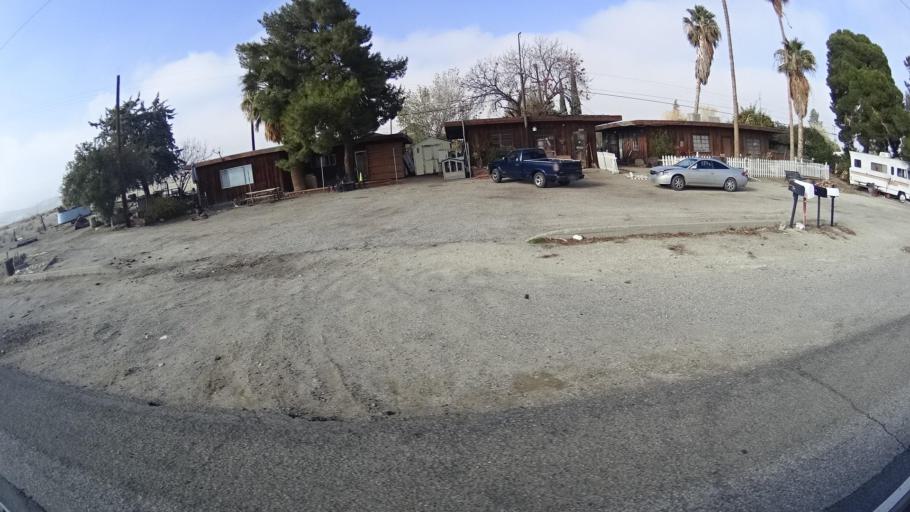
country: US
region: California
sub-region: Kern County
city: Maricopa
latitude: 35.0514
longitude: -119.4106
